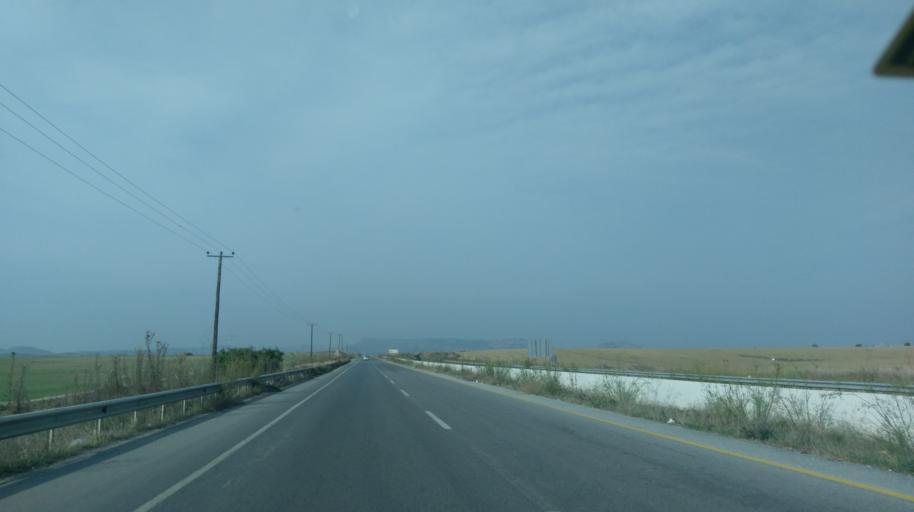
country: CY
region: Lefkosia
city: Mammari
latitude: 35.2107
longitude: 33.2165
